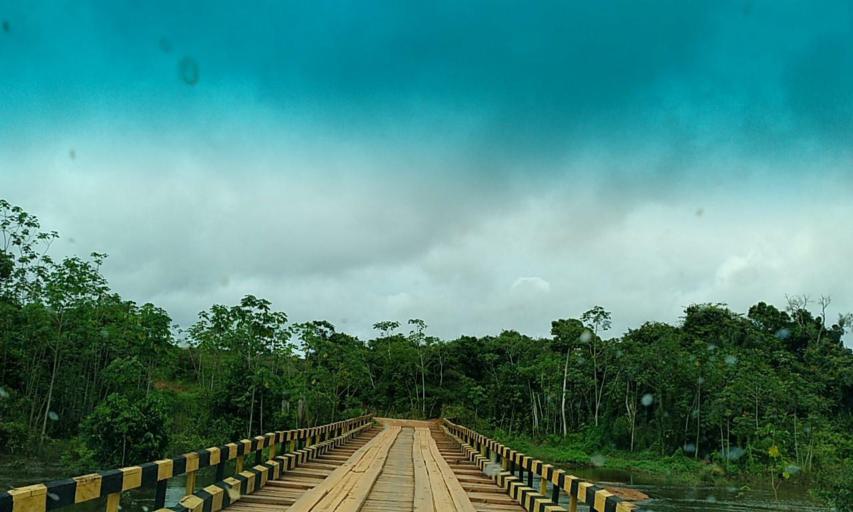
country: BR
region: Para
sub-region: Altamira
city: Altamira
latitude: -3.0796
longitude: -51.7029
